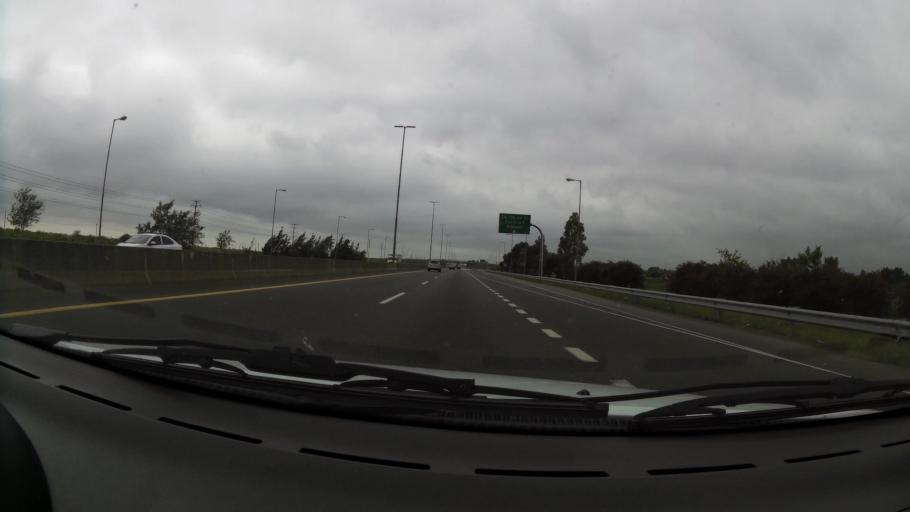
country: AR
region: Buenos Aires
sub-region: Partido de Quilmes
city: Quilmes
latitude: -34.7845
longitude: -58.1491
